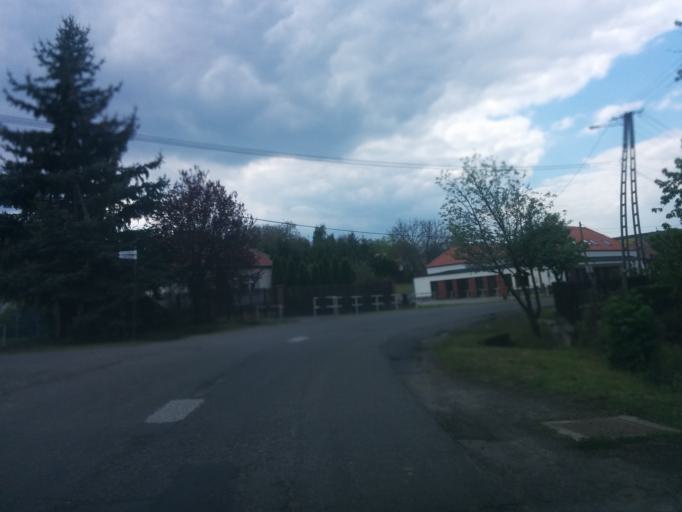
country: HU
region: Nograd
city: Bercel
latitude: 47.8250
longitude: 19.4501
